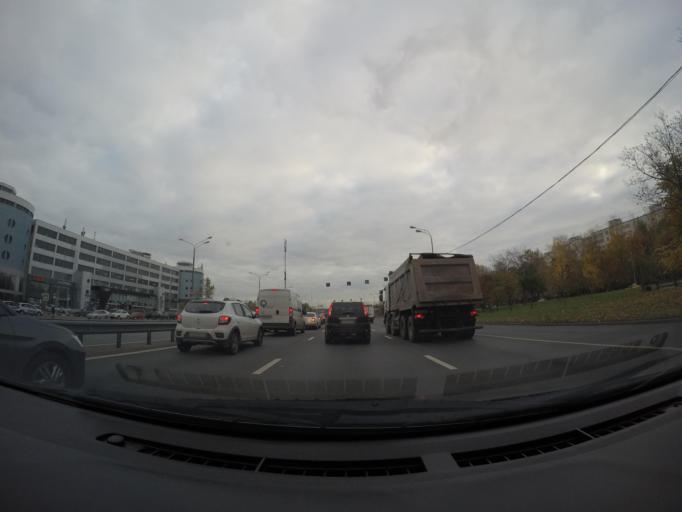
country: RU
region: Moscow
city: Ivanovskoye
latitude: 55.7746
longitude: 37.8330
